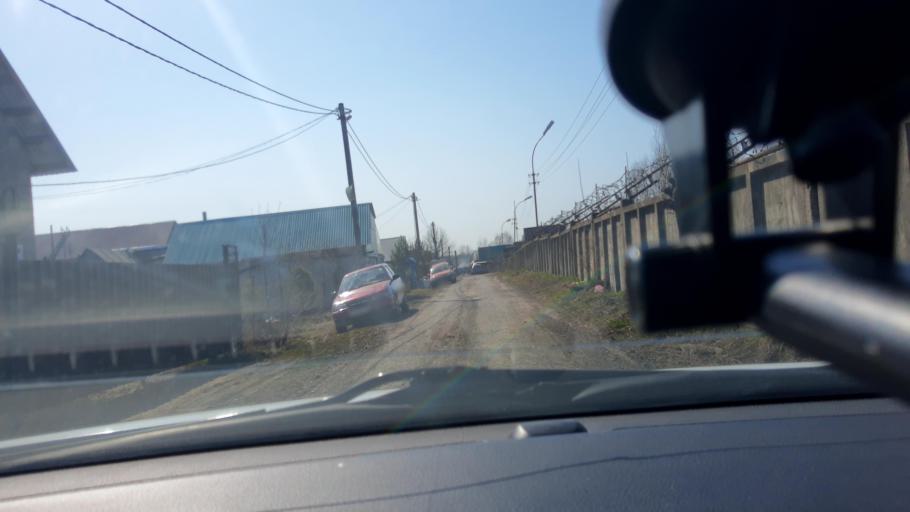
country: RU
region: Bashkortostan
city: Mikhaylovka
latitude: 54.7189
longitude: 55.8246
